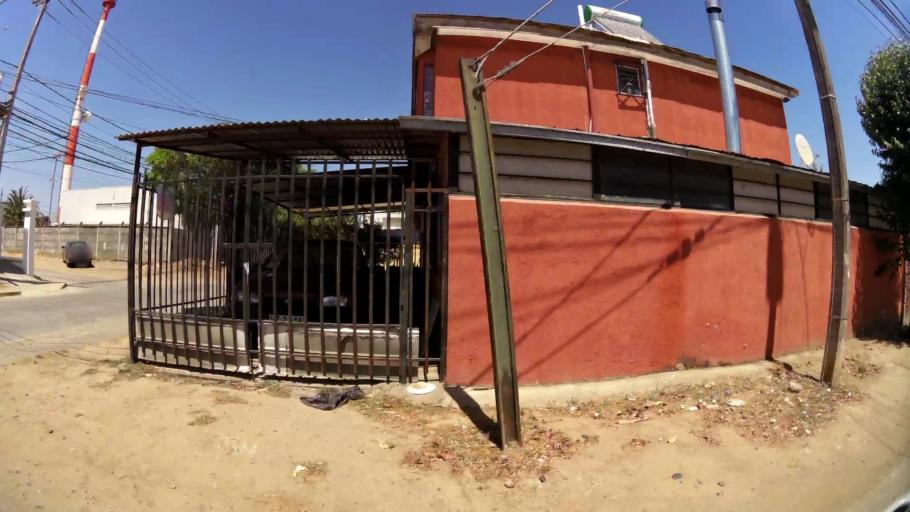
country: CL
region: Maule
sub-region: Provincia de Talca
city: Talca
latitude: -35.4311
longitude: -71.6324
